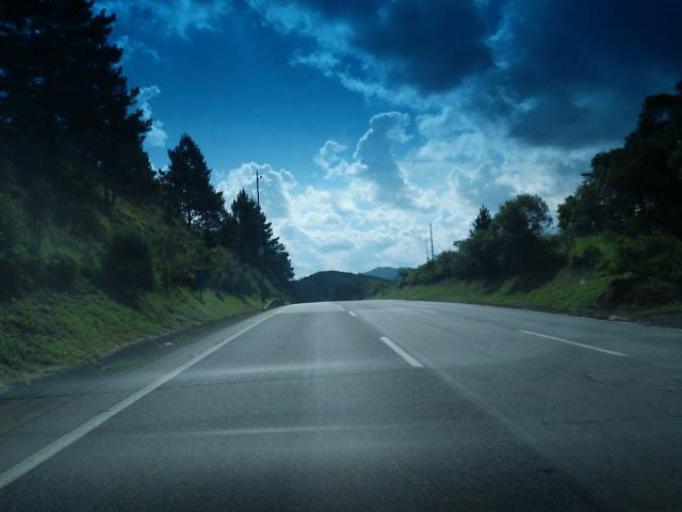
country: BR
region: Parana
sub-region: Campina Grande Do Sul
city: Campina Grande do Sul
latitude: -25.1051
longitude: -48.8402
